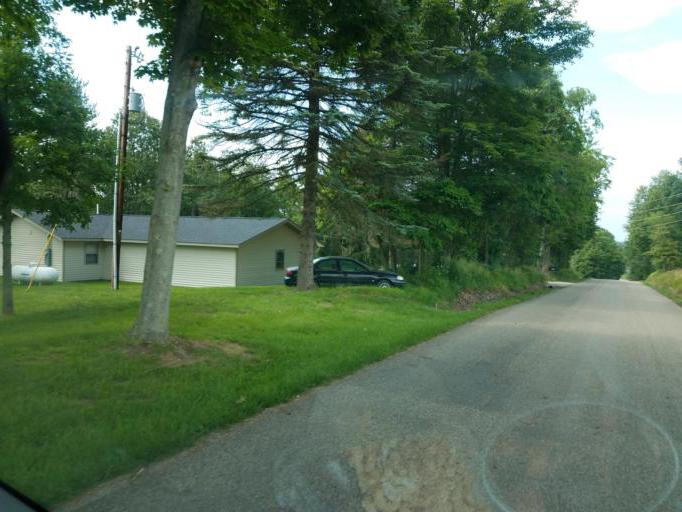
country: US
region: Ohio
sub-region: Knox County
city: Oak Hill
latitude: 40.2804
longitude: -82.2426
